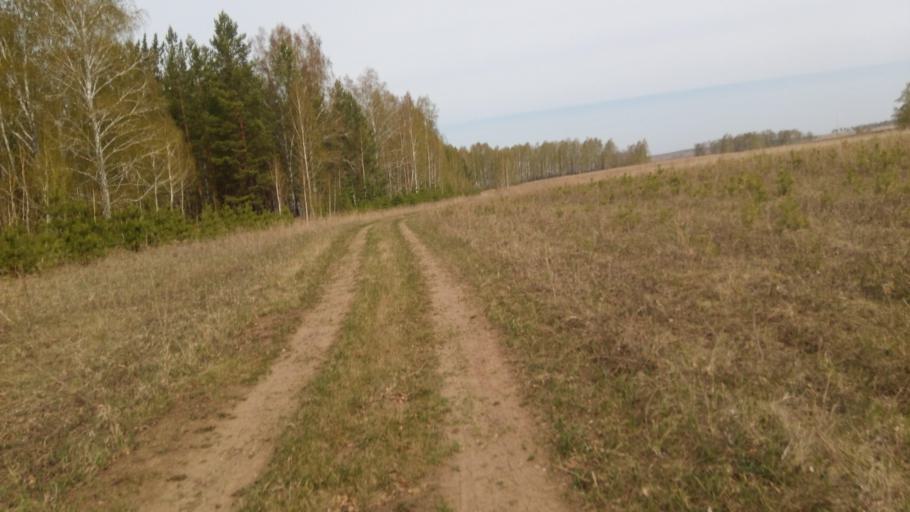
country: RU
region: Chelyabinsk
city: Timiryazevskiy
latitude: 55.0193
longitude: 60.8598
